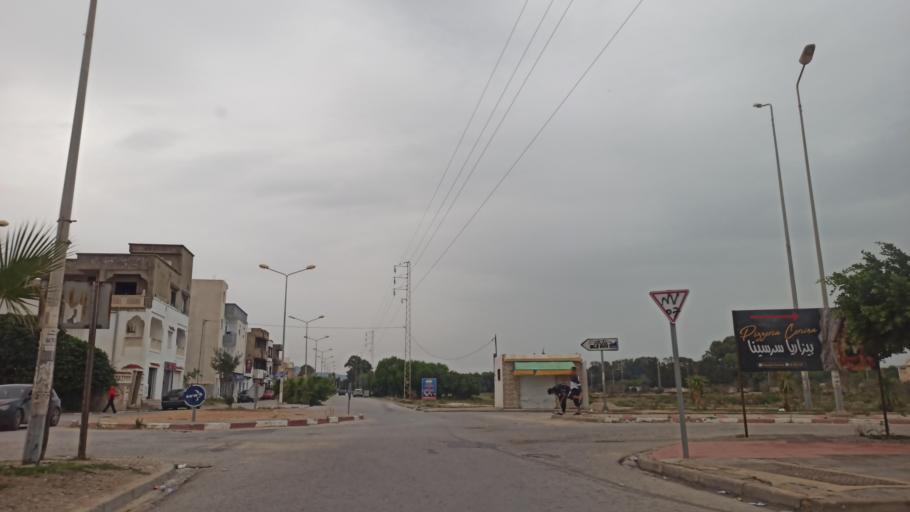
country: TN
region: Tunis
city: Hammam-Lif
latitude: 36.7092
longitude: 10.4121
